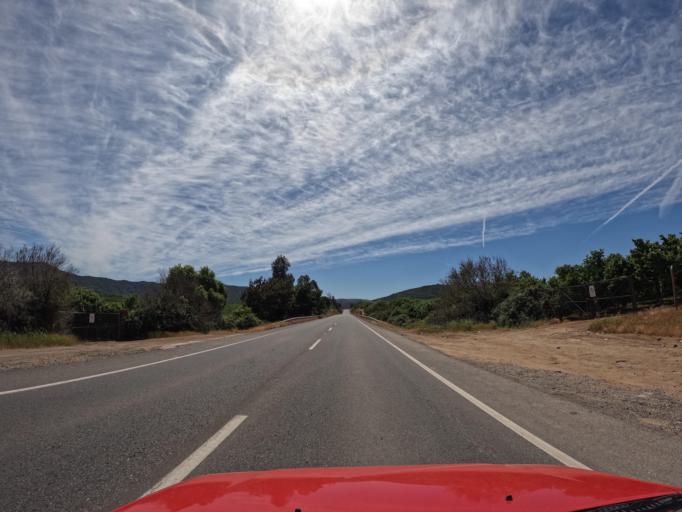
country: CL
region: Maule
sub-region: Provincia de Talca
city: Talca
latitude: -35.2734
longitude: -71.5392
